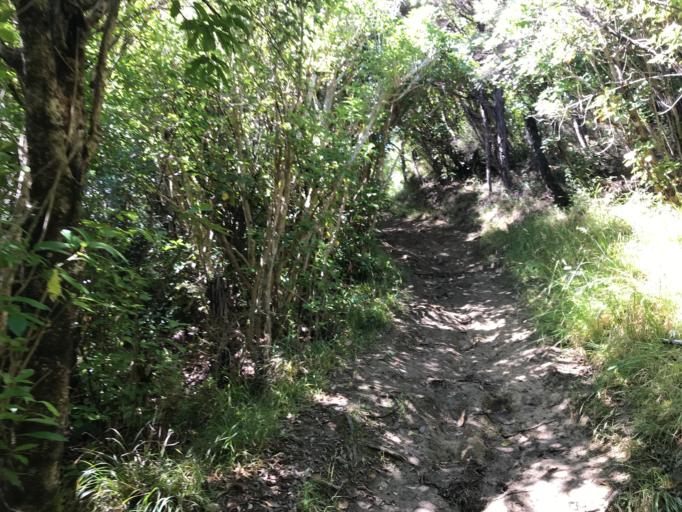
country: NZ
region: Marlborough
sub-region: Marlborough District
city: Picton
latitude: -41.2047
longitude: 174.0251
